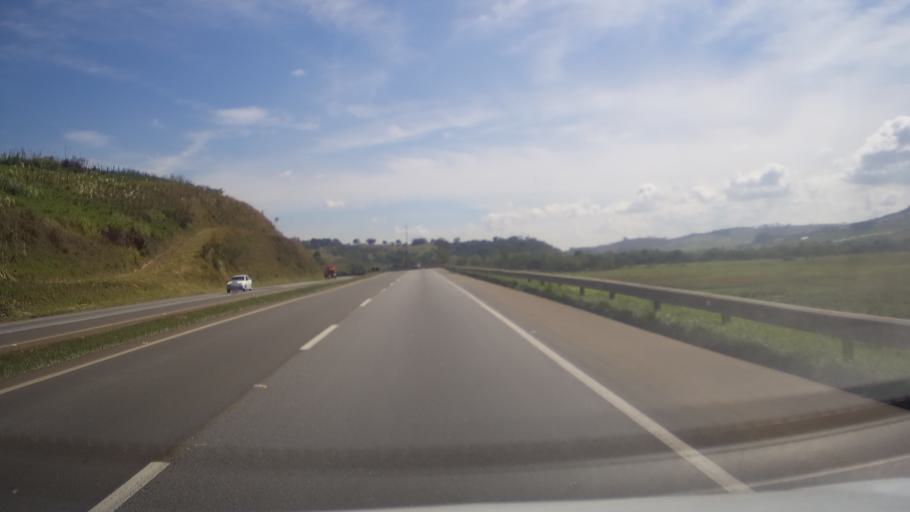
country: BR
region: Minas Gerais
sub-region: Cambui
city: Cambui
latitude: -22.5436
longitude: -46.0388
